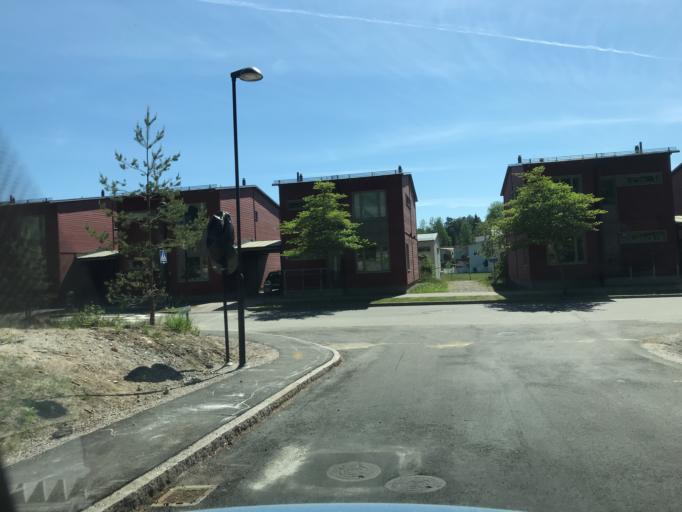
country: SE
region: Stockholm
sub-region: Solna Kommun
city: Rasunda
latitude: 59.4009
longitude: 17.9938
